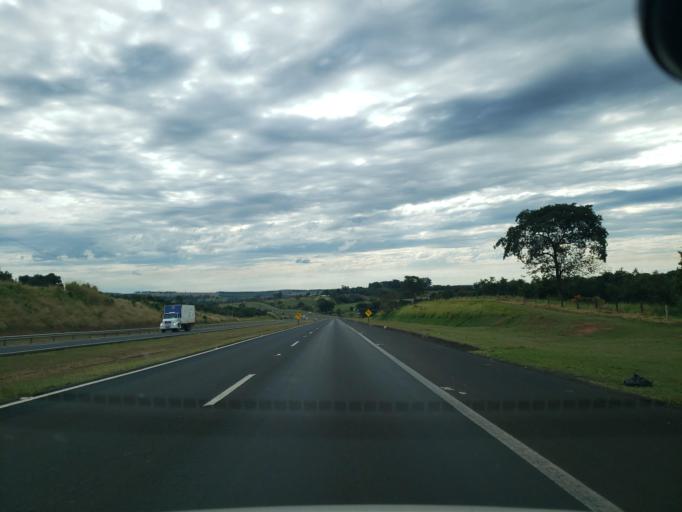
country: BR
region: Sao Paulo
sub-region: Bauru
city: Bauru
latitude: -22.2220
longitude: -49.1648
